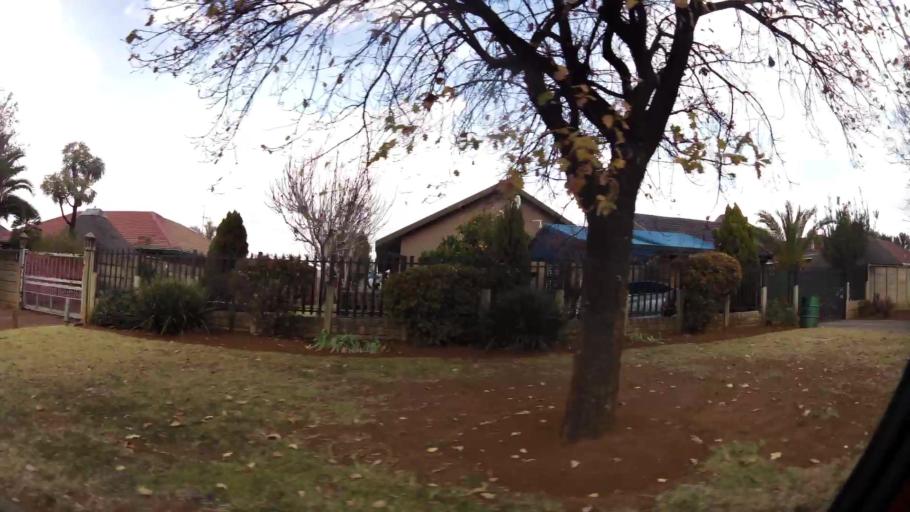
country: ZA
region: Gauteng
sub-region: Sedibeng District Municipality
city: Vanderbijlpark
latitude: -26.7177
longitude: 27.8535
